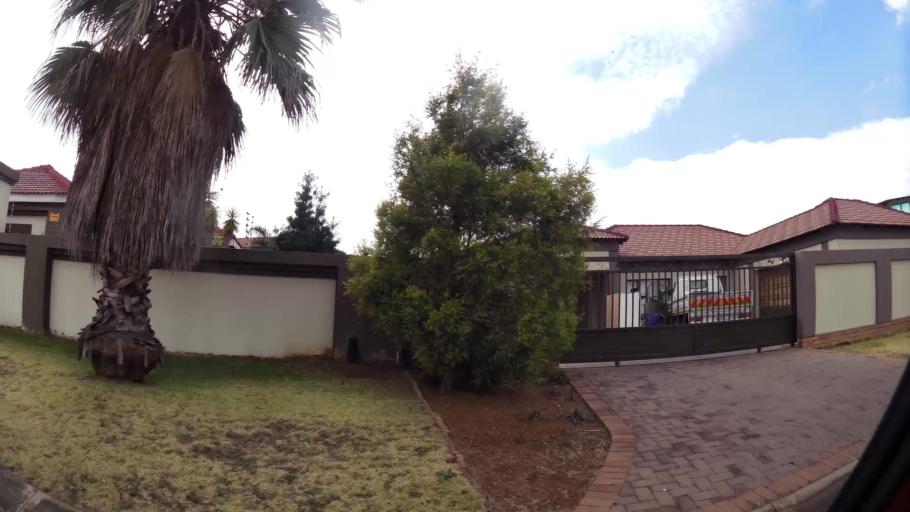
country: ZA
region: Gauteng
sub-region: Sedibeng District Municipality
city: Vanderbijlpark
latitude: -26.7246
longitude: 27.8678
